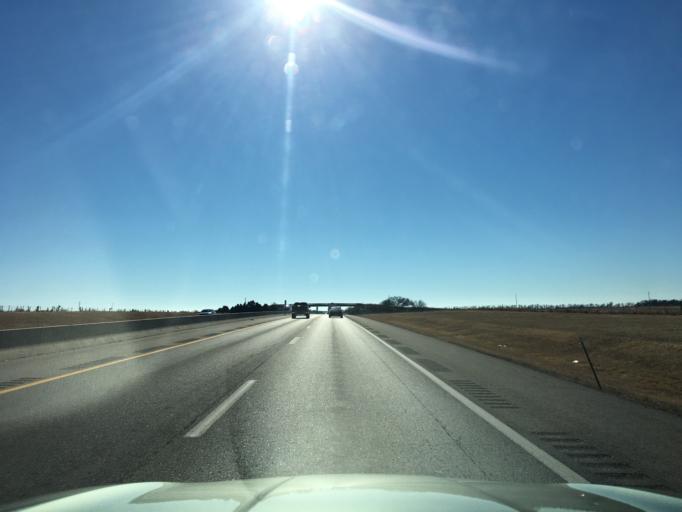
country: US
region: Kansas
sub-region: Sumner County
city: Wellington
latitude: 37.0462
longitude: -97.3383
